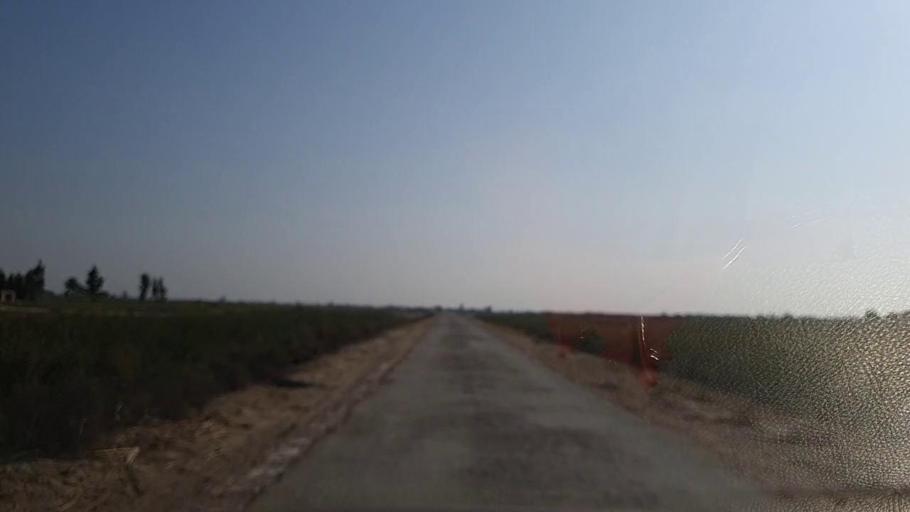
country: PK
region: Sindh
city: Sanghar
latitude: 26.0039
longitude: 69.0228
